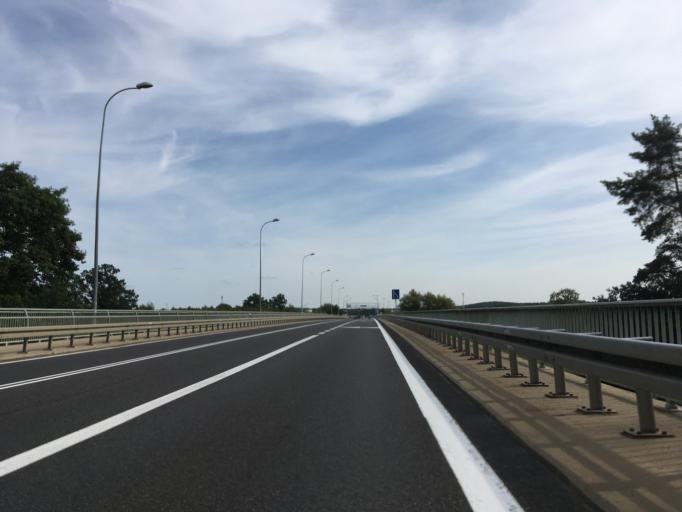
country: DE
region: Brandenburg
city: Guben
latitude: 51.9031
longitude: 14.6914
